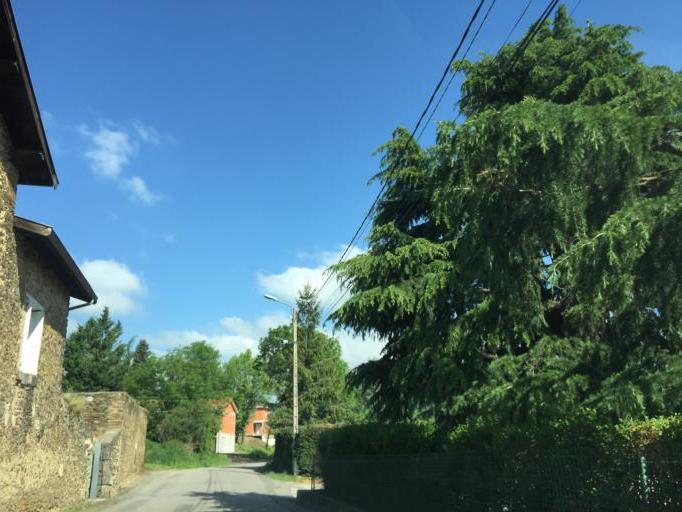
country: FR
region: Rhone-Alpes
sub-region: Departement de la Loire
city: Saint-Chamond
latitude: 45.4647
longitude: 4.5361
